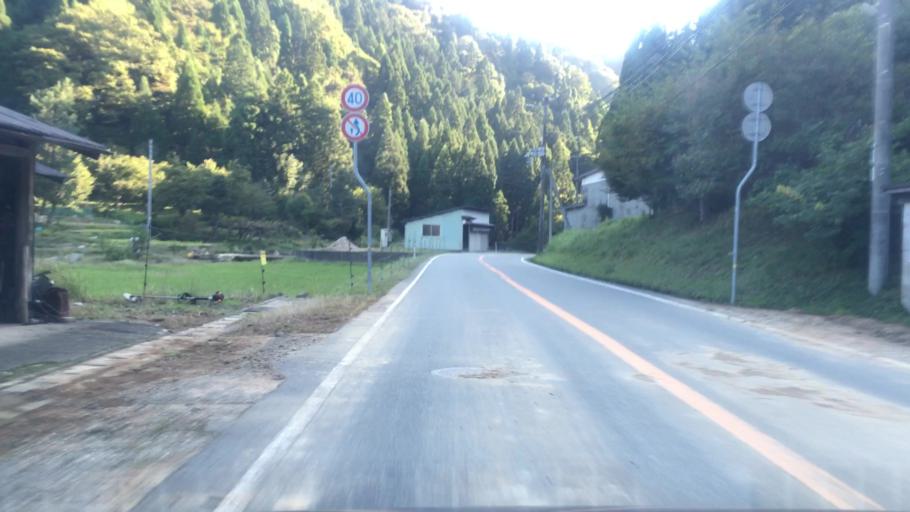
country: JP
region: Hyogo
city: Toyooka
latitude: 35.6205
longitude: 134.8619
